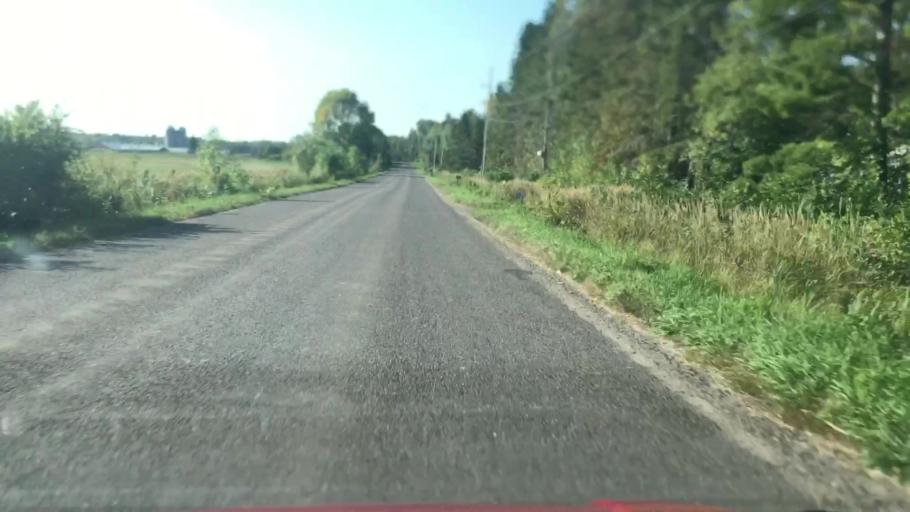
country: US
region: Michigan
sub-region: Chippewa County
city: Sault Ste. Marie
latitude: 46.2899
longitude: -84.0631
